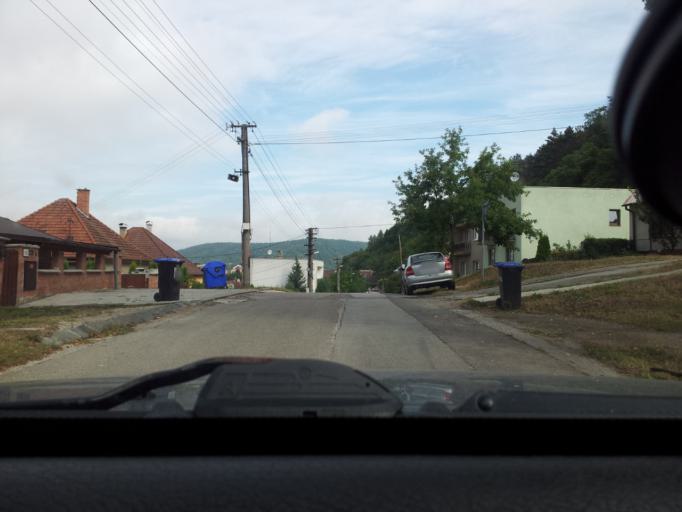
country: SK
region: Trenciansky
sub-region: Okres Trencin
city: Trencin
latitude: 48.8918
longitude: 18.0889
